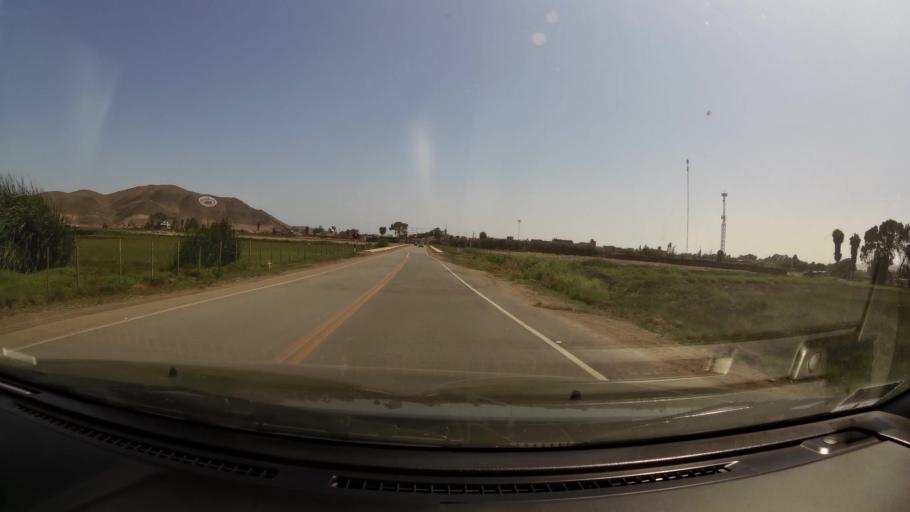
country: PE
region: Lima
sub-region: Provincia de Canete
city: San Vicente de Canete
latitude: -13.0298
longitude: -76.4762
